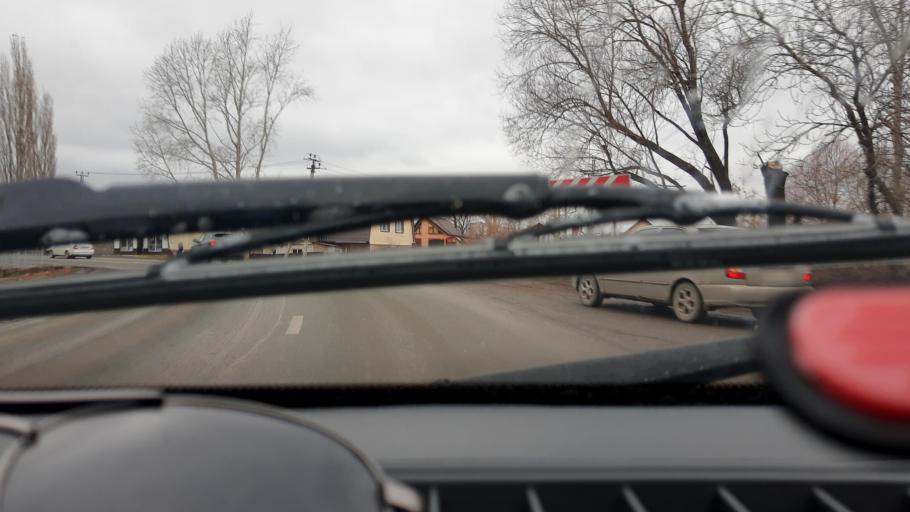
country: RU
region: Bashkortostan
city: Avdon
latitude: 54.7118
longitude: 55.8179
